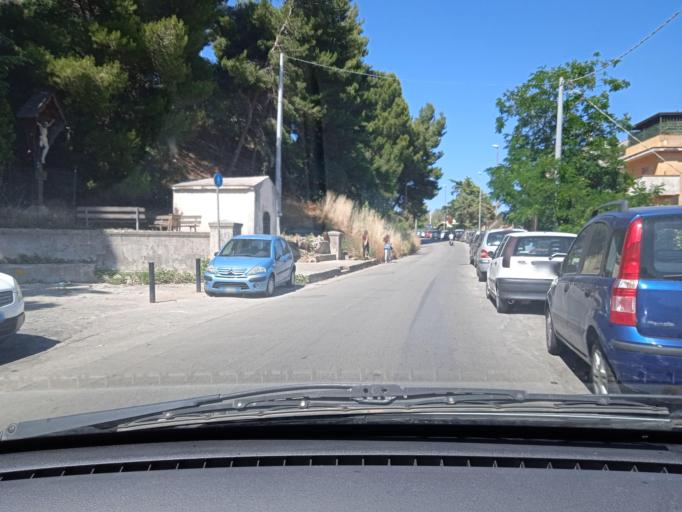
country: IT
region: Sicily
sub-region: Palermo
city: Monreale
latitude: 38.0771
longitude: 13.2804
